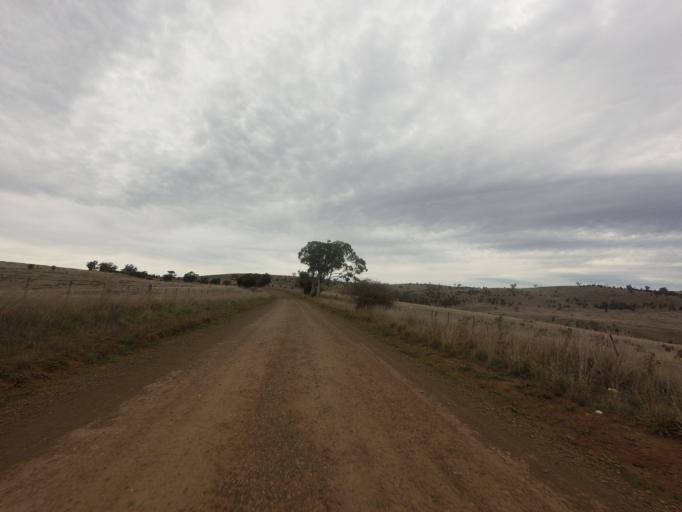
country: AU
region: Tasmania
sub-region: Derwent Valley
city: New Norfolk
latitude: -42.5570
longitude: 146.8863
